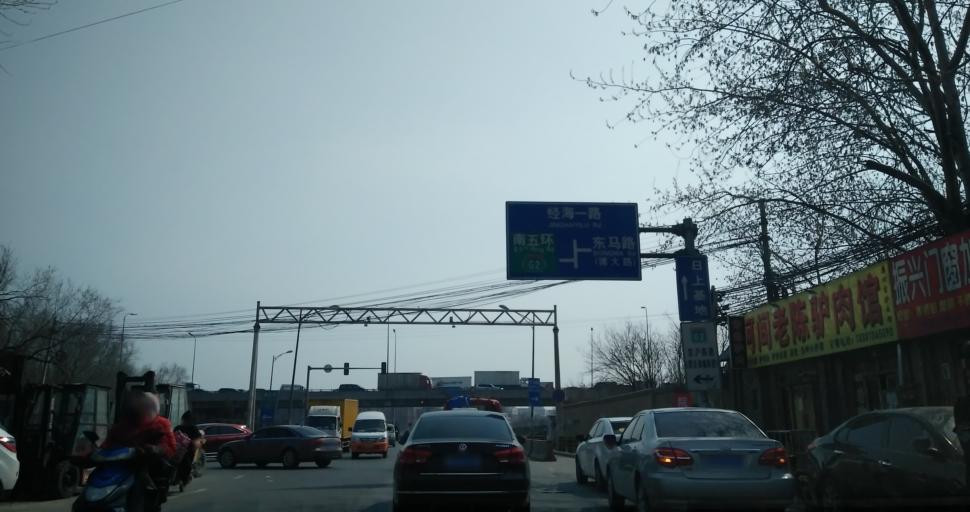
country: CN
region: Beijing
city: Jiugong
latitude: 39.8221
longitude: 116.5051
